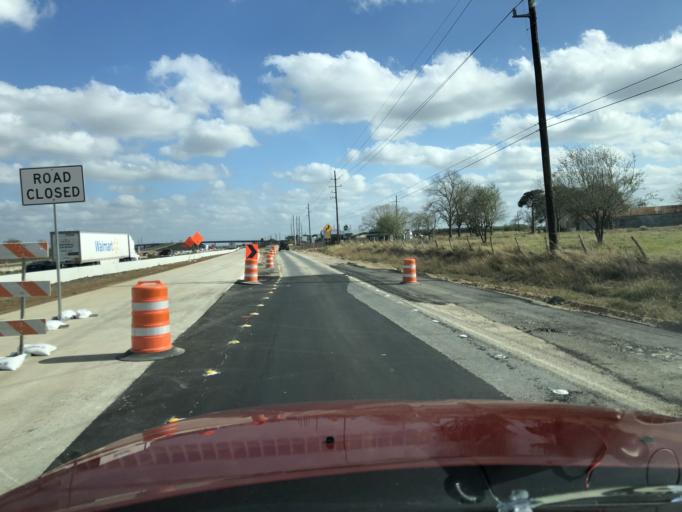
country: US
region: Texas
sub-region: Austin County
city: Sealy
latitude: 29.7737
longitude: -96.0825
